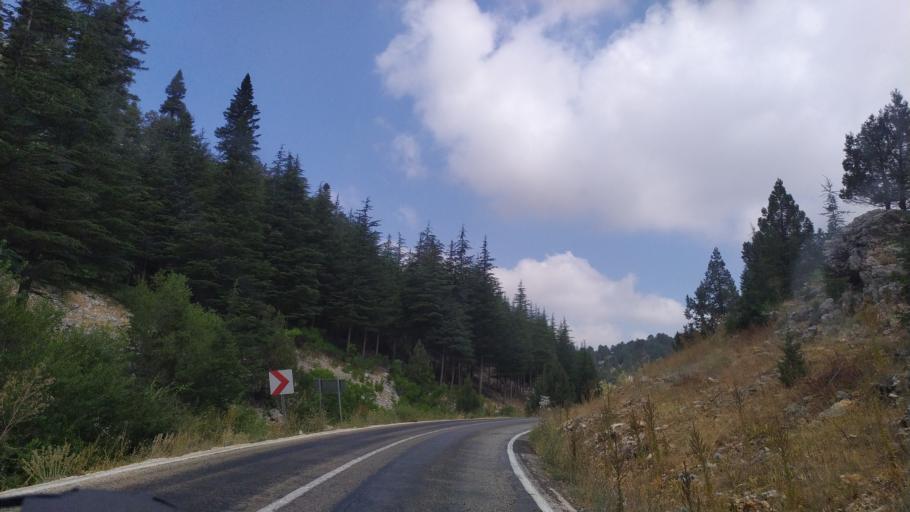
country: TR
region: Mersin
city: Kirobasi
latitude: 36.6123
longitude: 33.8798
